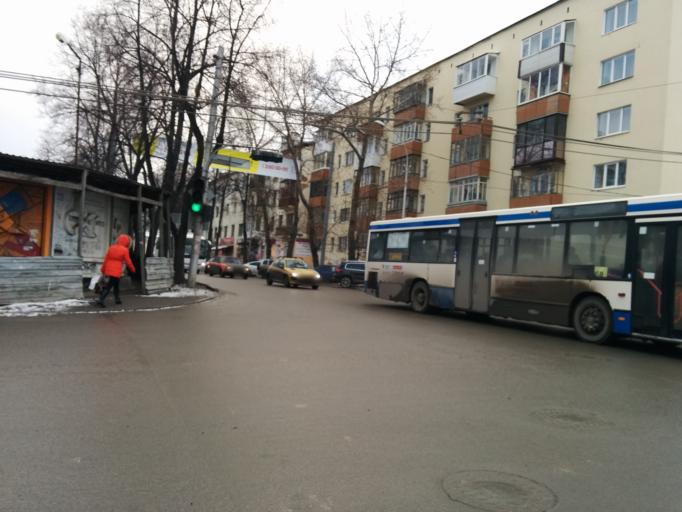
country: RU
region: Perm
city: Perm
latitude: 58.0106
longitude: 56.2449
